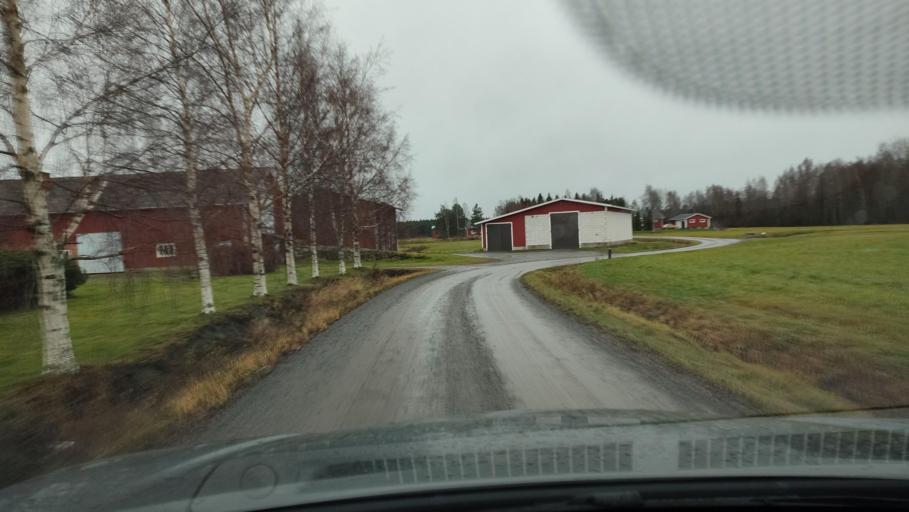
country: FI
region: Southern Ostrobothnia
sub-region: Suupohja
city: Karijoki
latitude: 62.2391
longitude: 21.5510
